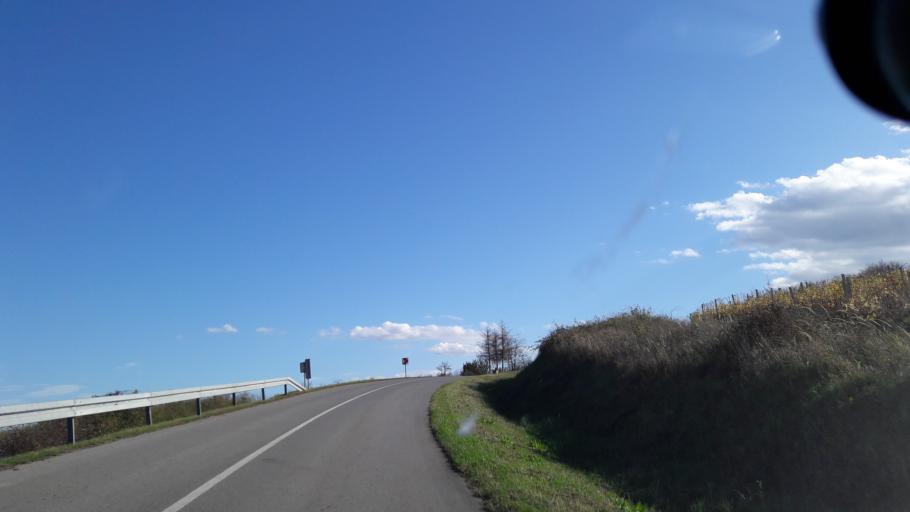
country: HR
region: Osjecko-Baranjska
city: Gorjani
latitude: 45.3887
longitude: 18.2481
